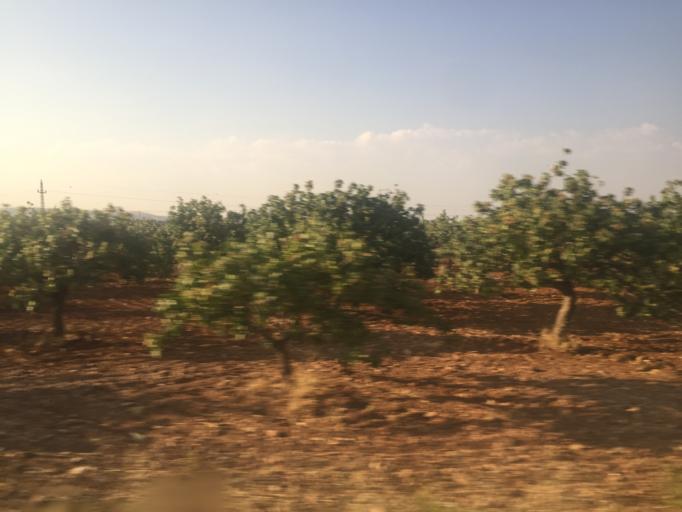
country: TR
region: Gaziantep
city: Nizip
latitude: 37.0142
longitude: 37.8455
